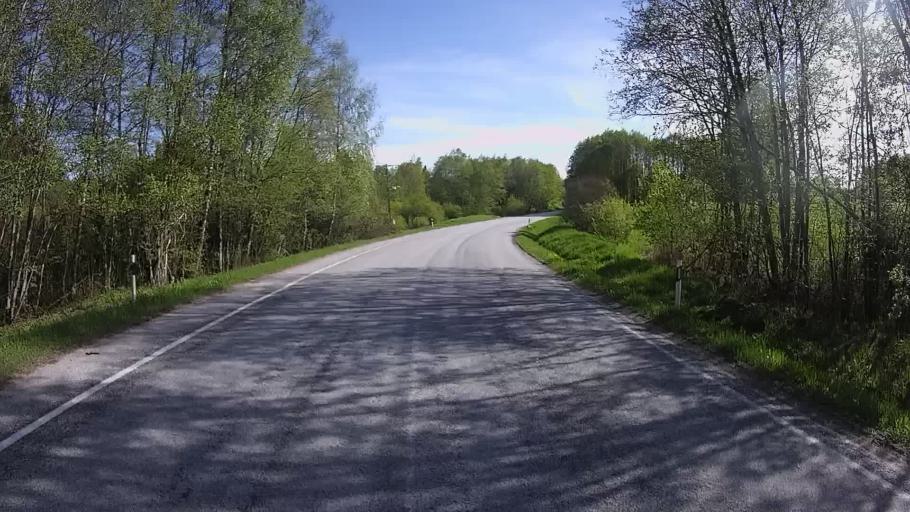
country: EE
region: Vorumaa
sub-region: Antsla vald
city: Vana-Antsla
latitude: 58.0286
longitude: 26.5103
